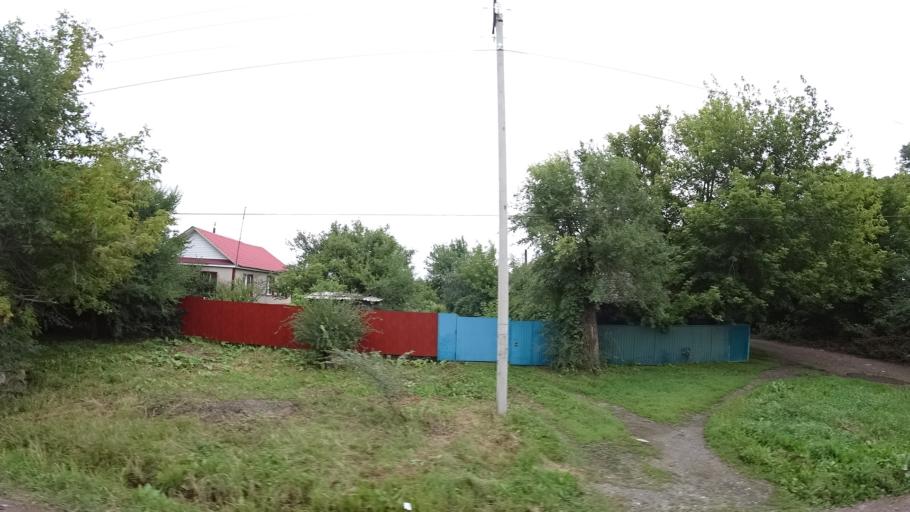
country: RU
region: Primorskiy
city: Chernigovka
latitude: 44.3393
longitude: 132.5901
